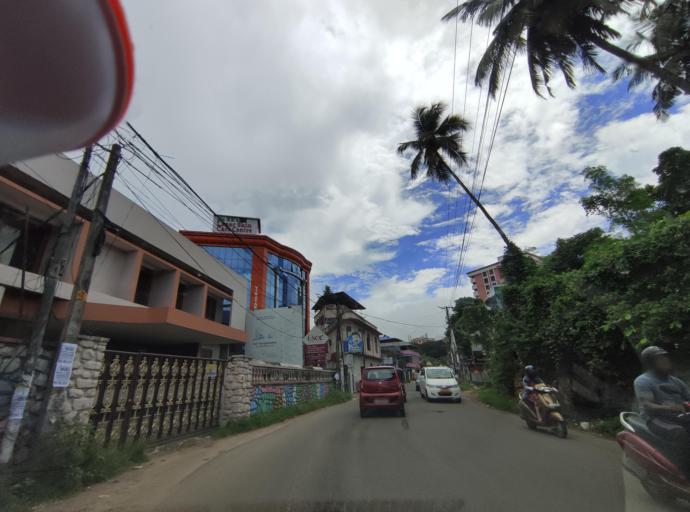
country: IN
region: Kerala
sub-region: Thiruvananthapuram
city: Thiruvananthapuram
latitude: 8.4944
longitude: 76.9639
